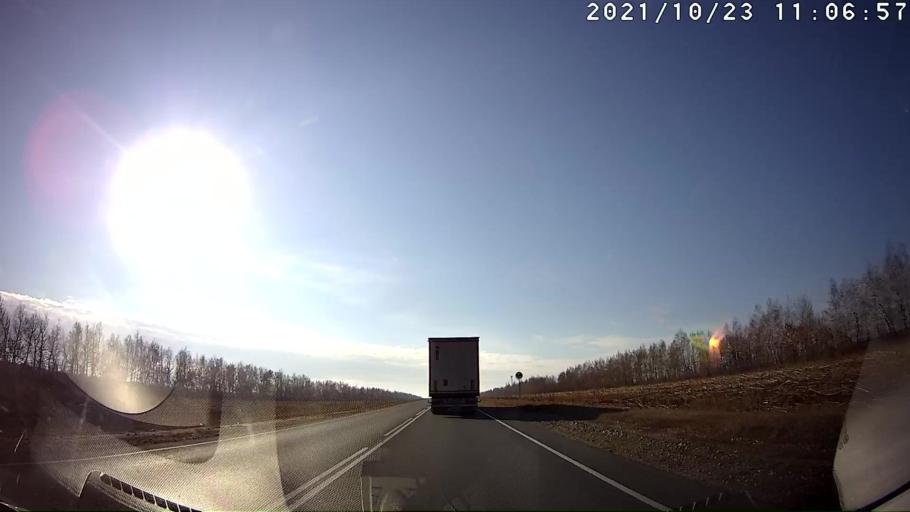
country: RU
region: Saratov
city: Krasnoarmeysk
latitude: 51.0462
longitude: 45.6306
